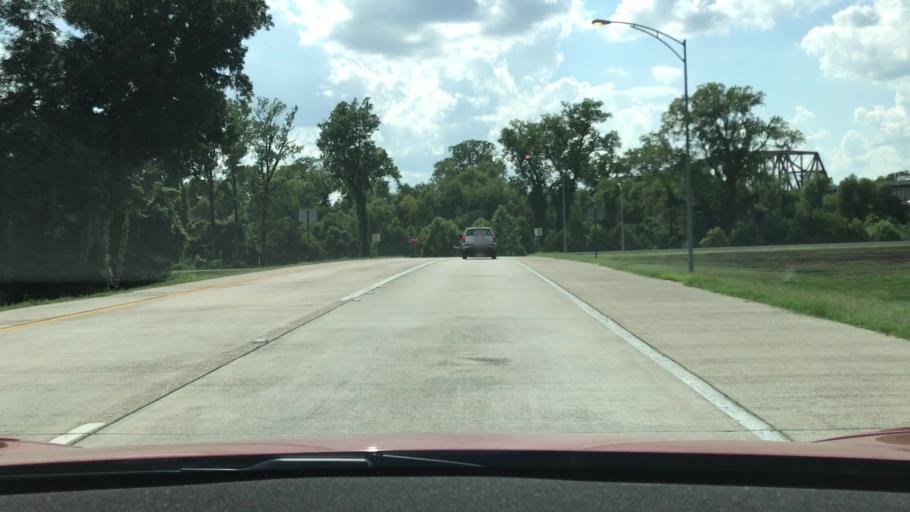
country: US
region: Louisiana
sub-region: Bossier Parish
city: Bossier City
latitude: 32.4578
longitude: -93.6744
